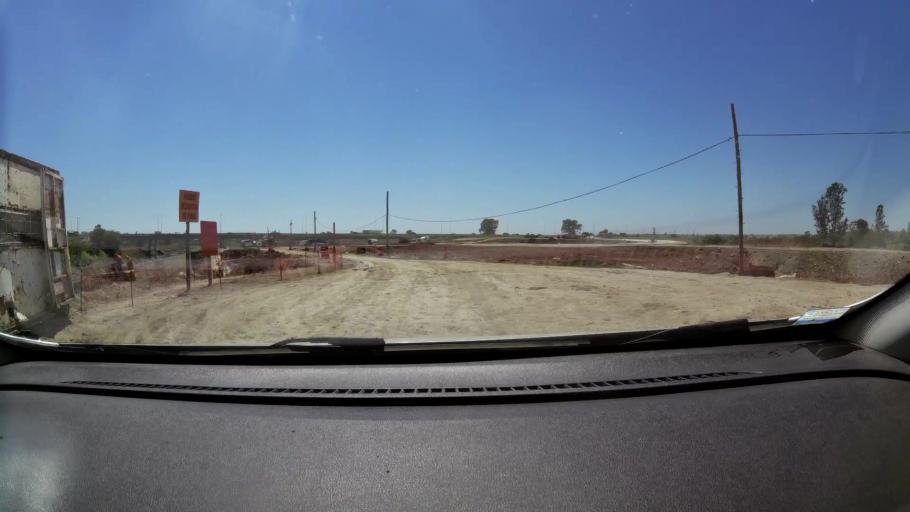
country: AR
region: Cordoba
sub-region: Departamento de Capital
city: Cordoba
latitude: -31.4082
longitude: -64.1258
